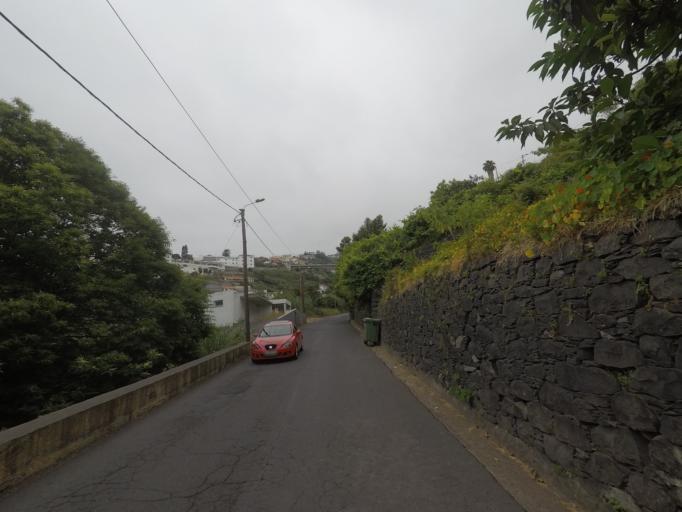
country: PT
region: Madeira
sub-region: Funchal
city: Nossa Senhora do Monte
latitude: 32.6753
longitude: -16.9436
